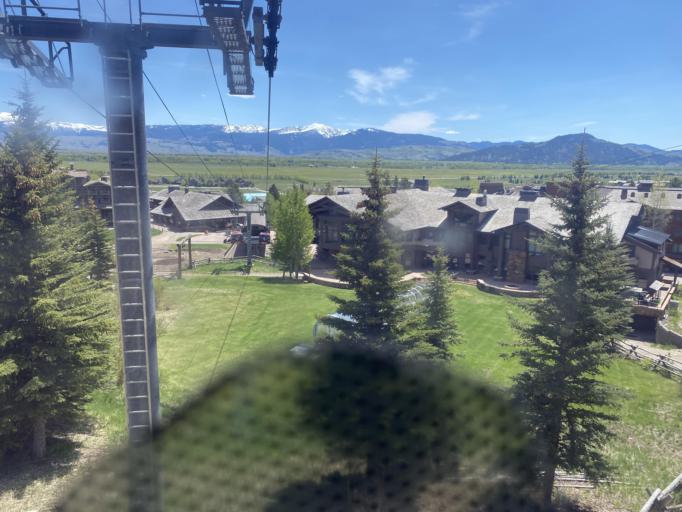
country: US
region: Wyoming
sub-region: Teton County
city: Moose Wilson Road
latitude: 43.5894
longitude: -110.8294
